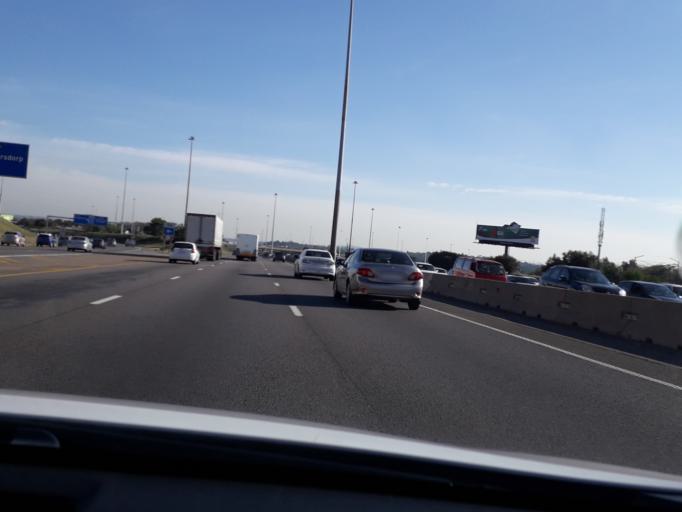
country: ZA
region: Gauteng
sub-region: City of Tshwane Metropolitan Municipality
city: Centurion
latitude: -25.8860
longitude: 28.1663
